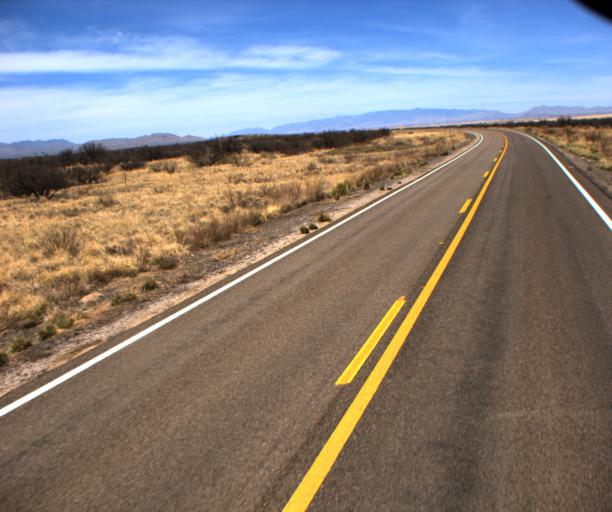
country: US
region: Arizona
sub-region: Cochise County
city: Willcox
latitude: 32.1254
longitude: -109.9088
